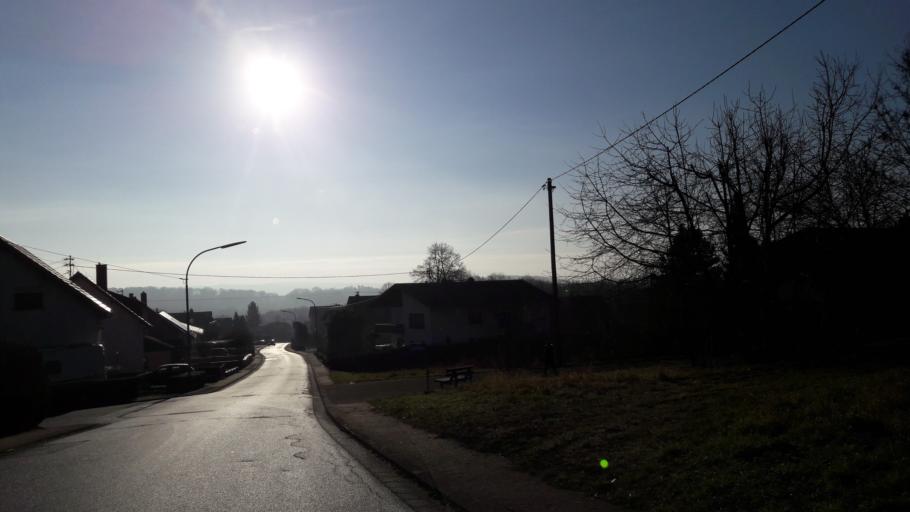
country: DE
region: Saarland
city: Tholey
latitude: 49.4794
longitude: 7.0266
